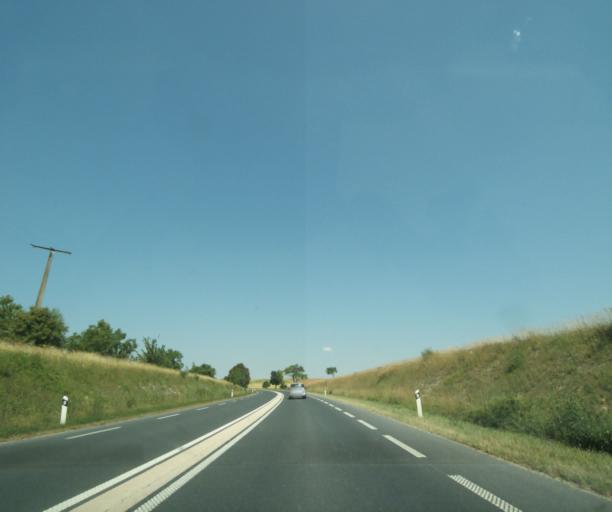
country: FR
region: Champagne-Ardenne
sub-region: Departement de la Marne
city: Mourmelon-le-Grand
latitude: 49.0686
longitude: 4.2954
